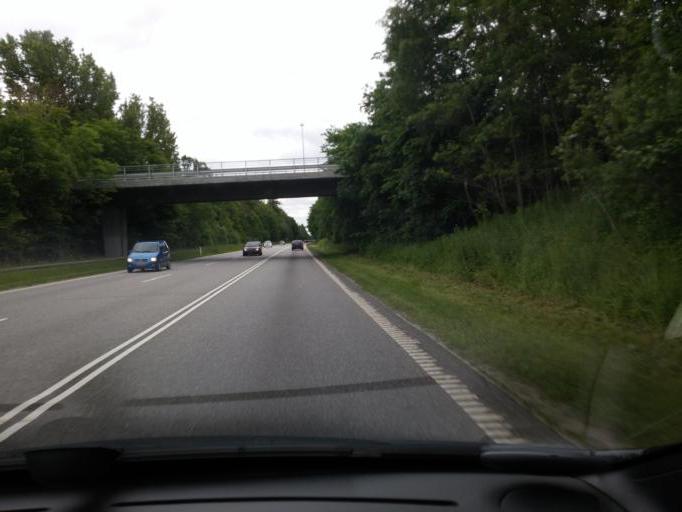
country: DK
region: Capital Region
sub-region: Hillerod Kommune
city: Hillerod
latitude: 55.8899
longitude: 12.2920
